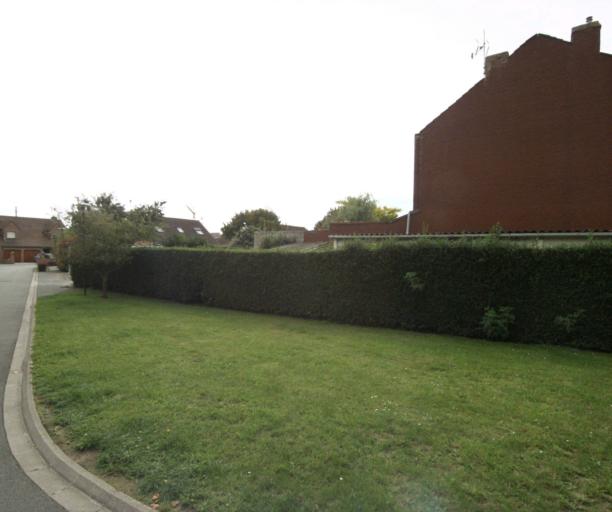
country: FR
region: Nord-Pas-de-Calais
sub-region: Departement du Nord
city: Templemars
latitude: 50.5833
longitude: 3.0531
